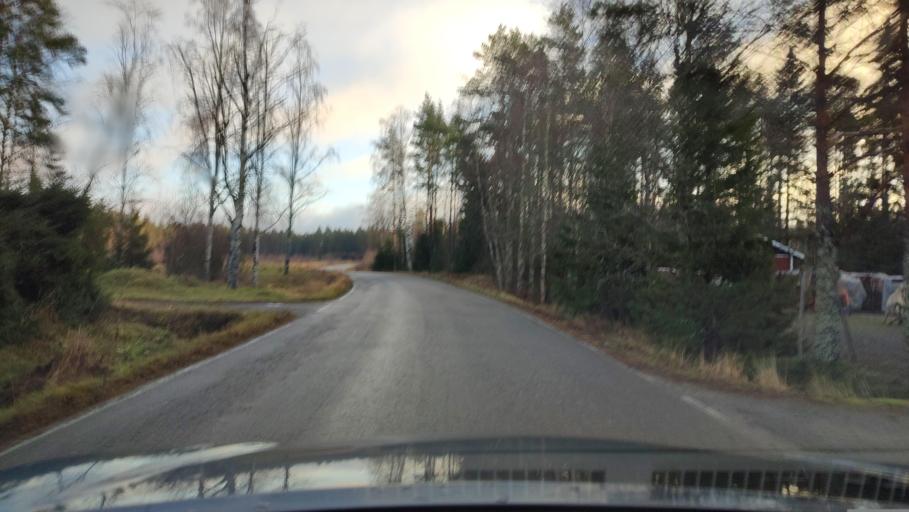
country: FI
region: Ostrobothnia
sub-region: Sydosterbotten
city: Naerpes
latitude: 62.4428
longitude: 21.3818
